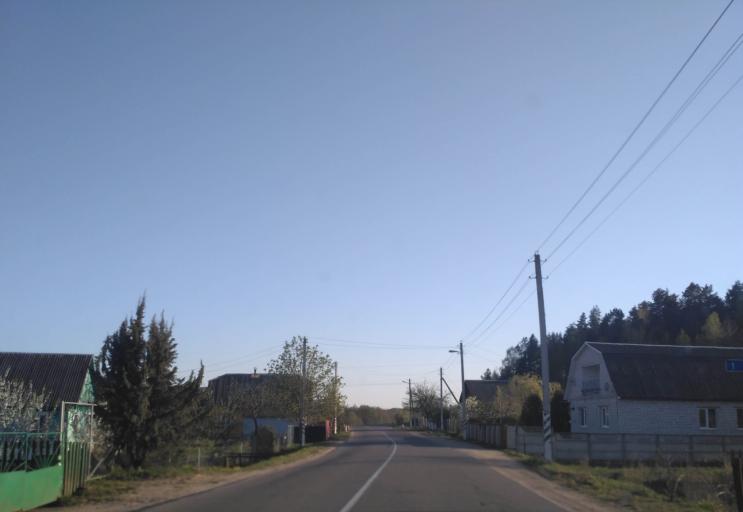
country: BY
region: Minsk
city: Radashkovichy
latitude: 54.1497
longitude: 27.2166
